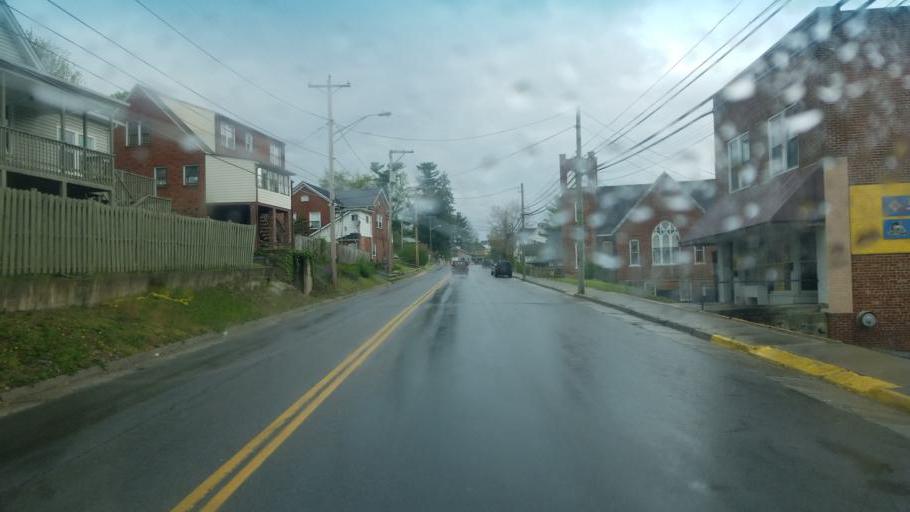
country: US
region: Virginia
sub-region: Smyth County
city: Marion
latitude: 36.8302
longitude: -81.5248
